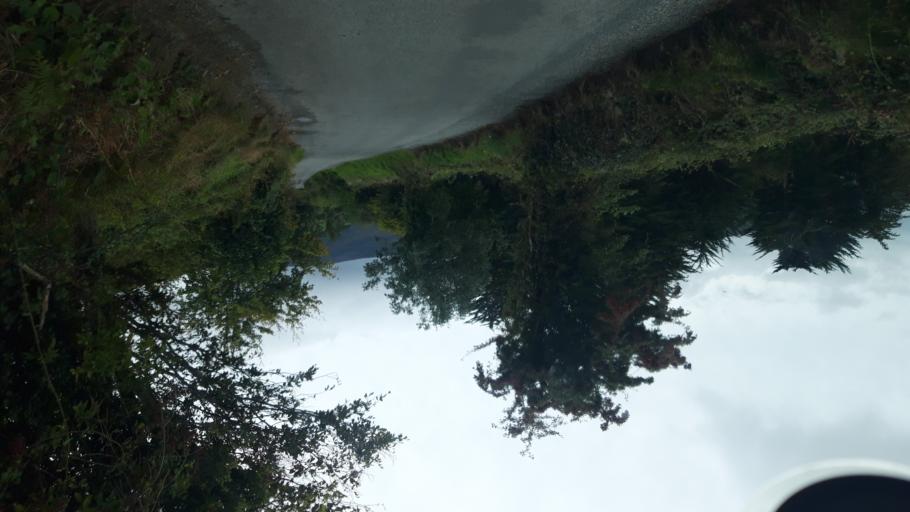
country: IE
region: Leinster
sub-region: Wicklow
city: Enniskerry
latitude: 53.1849
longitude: -6.2042
